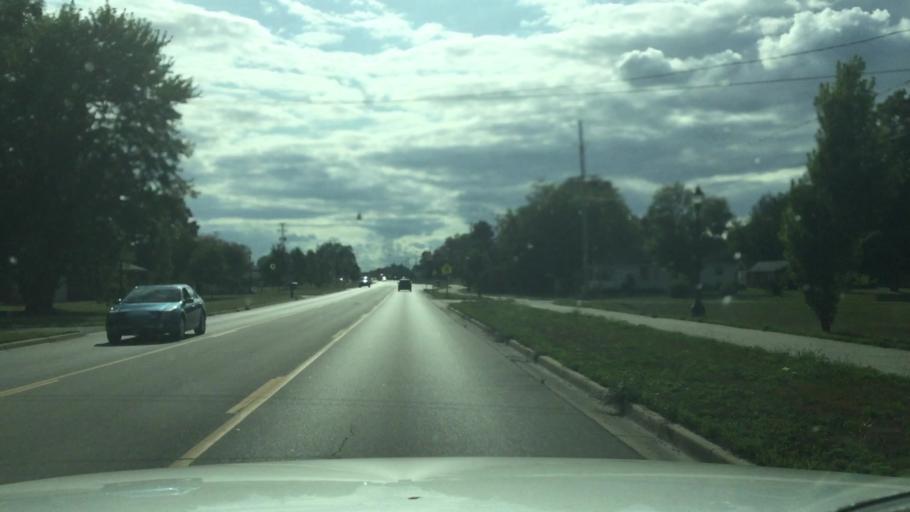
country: US
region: Michigan
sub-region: Ionia County
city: Belding
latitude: 43.0889
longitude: -85.2482
